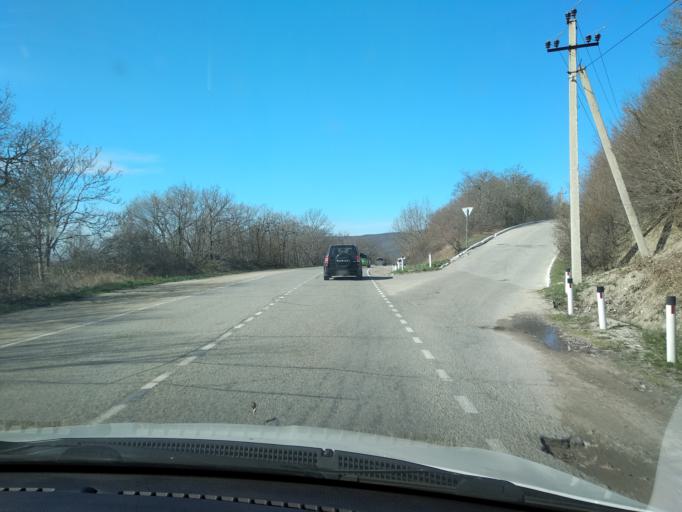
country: RU
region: Krasnodarskiy
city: Novorossiysk
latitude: 44.7113
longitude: 37.7269
